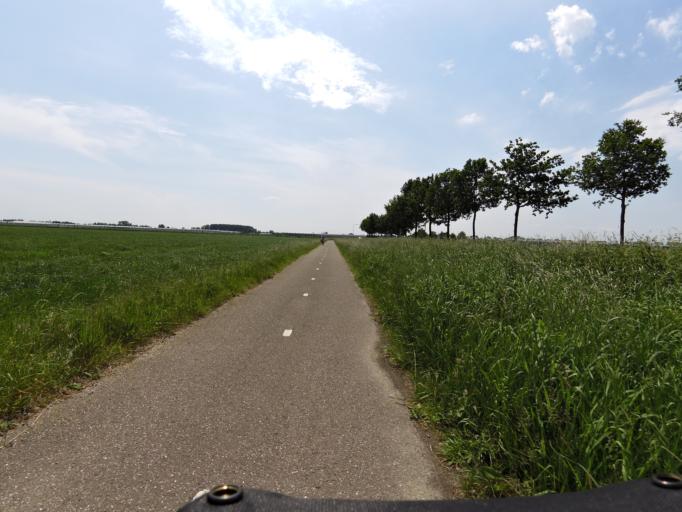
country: NL
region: North Brabant
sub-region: Gemeente Aalburg
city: Aalburg
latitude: 51.7975
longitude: 5.0832
